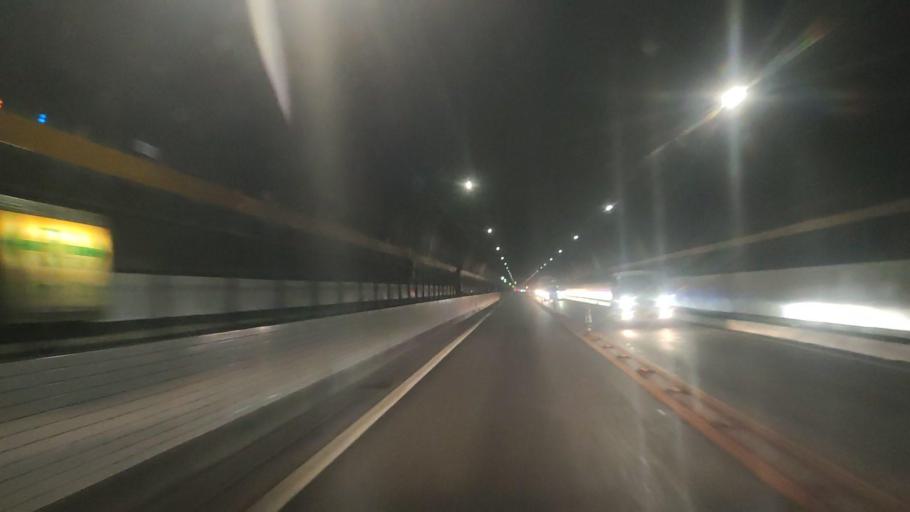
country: JP
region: Nagasaki
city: Obita
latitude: 32.7857
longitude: 129.8832
